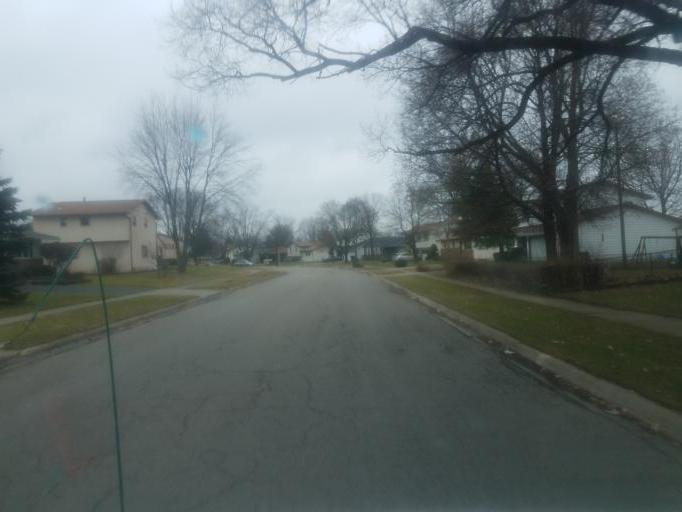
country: US
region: Ohio
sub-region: Franklin County
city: Minerva Park
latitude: 40.0806
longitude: -82.9691
